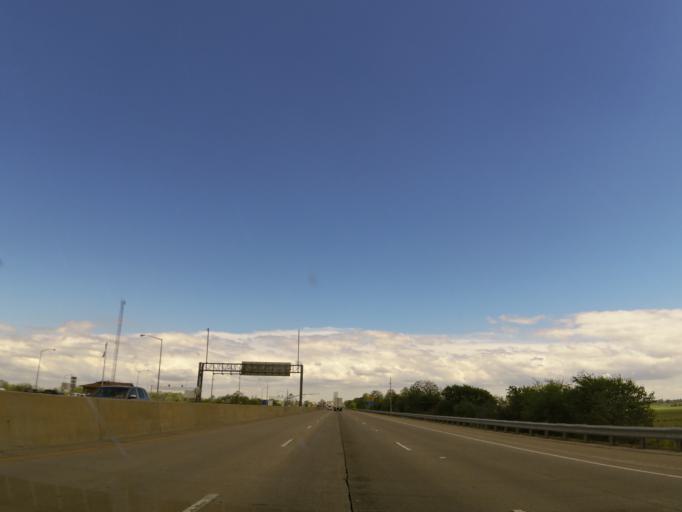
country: US
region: Tennessee
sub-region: Shelby County
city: Memphis
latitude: 35.1531
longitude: -90.0904
